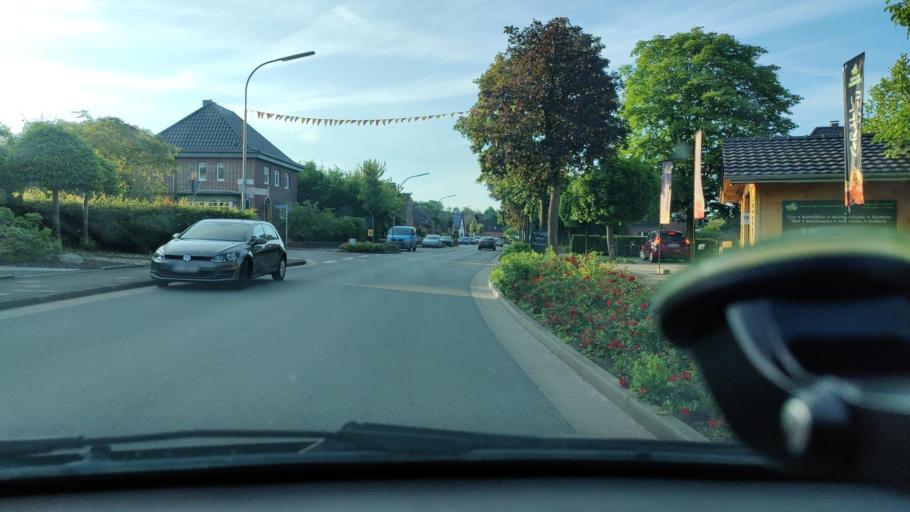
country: DE
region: North Rhine-Westphalia
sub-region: Regierungsbezirk Dusseldorf
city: Rheurdt
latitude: 51.4706
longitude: 6.4672
